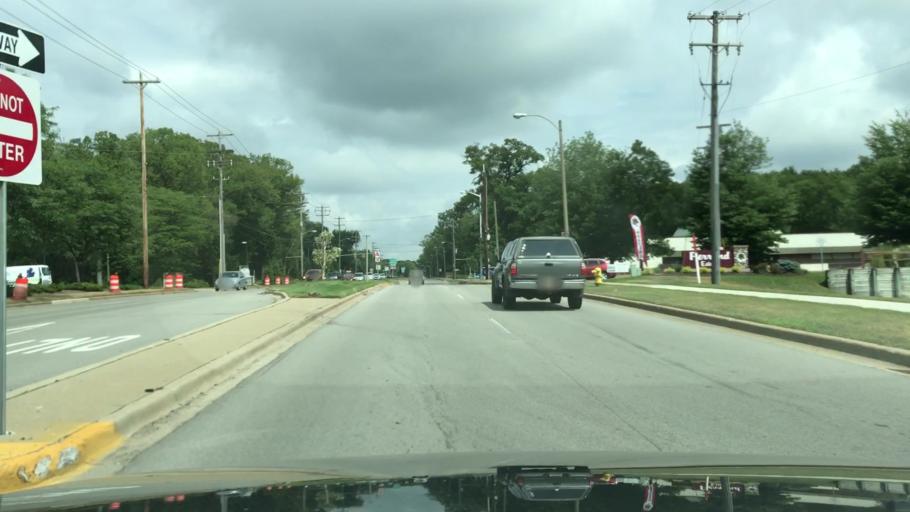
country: US
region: Michigan
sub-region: Kent County
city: Wyoming
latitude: 42.8846
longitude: -85.7315
